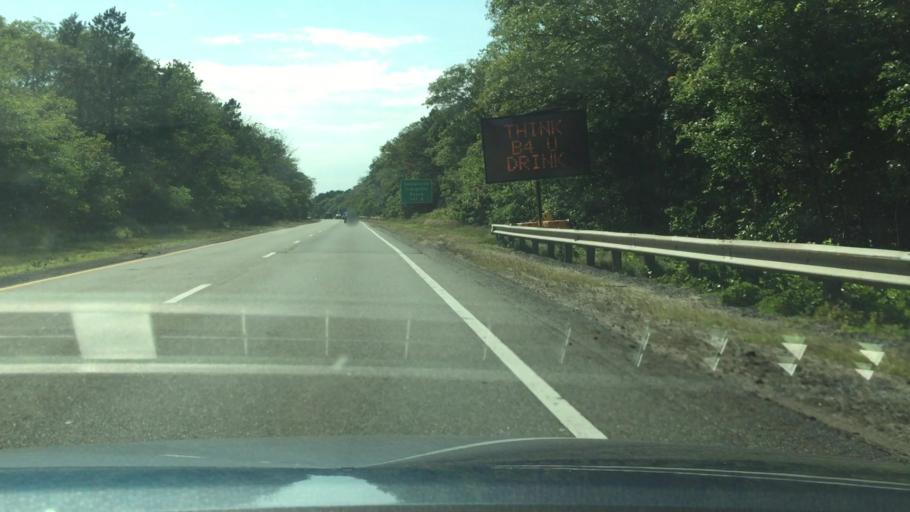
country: US
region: Massachusetts
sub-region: Barnstable County
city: Barnstable
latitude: 41.6895
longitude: -70.3108
